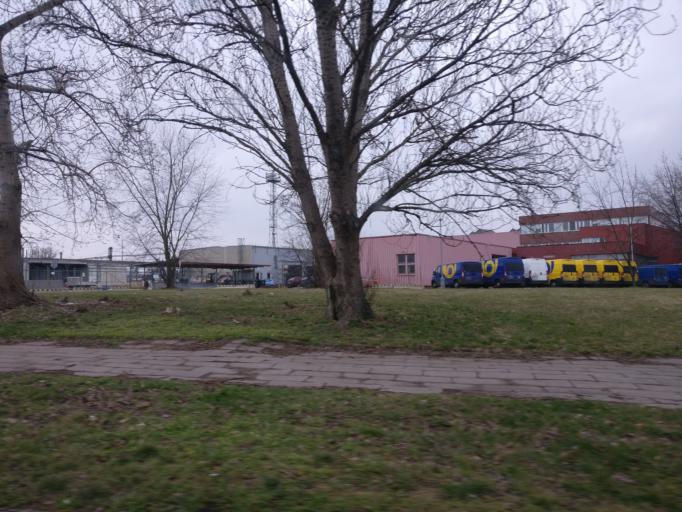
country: CZ
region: Pardubicky
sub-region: Okres Pardubice
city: Pardubice
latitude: 50.0331
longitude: 15.7614
